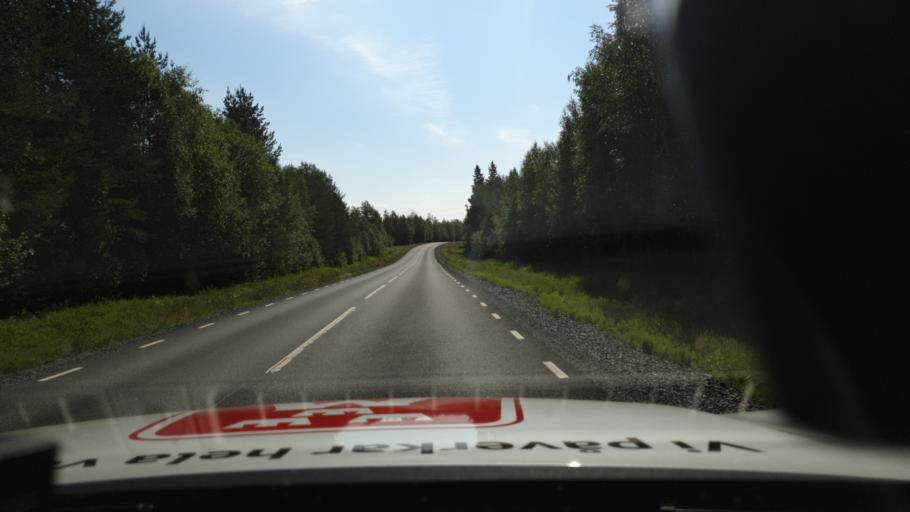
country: SE
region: Norrbotten
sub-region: Bodens Kommun
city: Saevast
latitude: 65.8436
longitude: 21.7954
